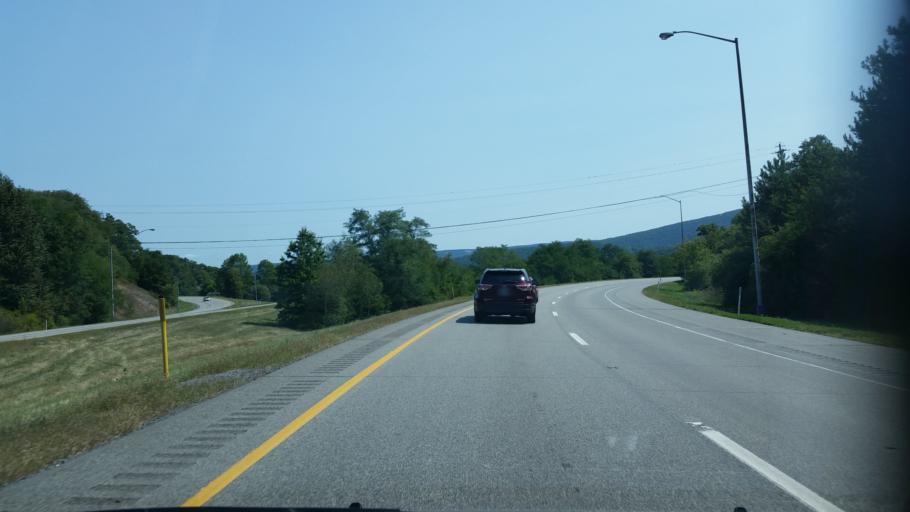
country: US
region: Pennsylvania
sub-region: Blair County
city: Duncansville
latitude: 40.4405
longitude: -78.4333
